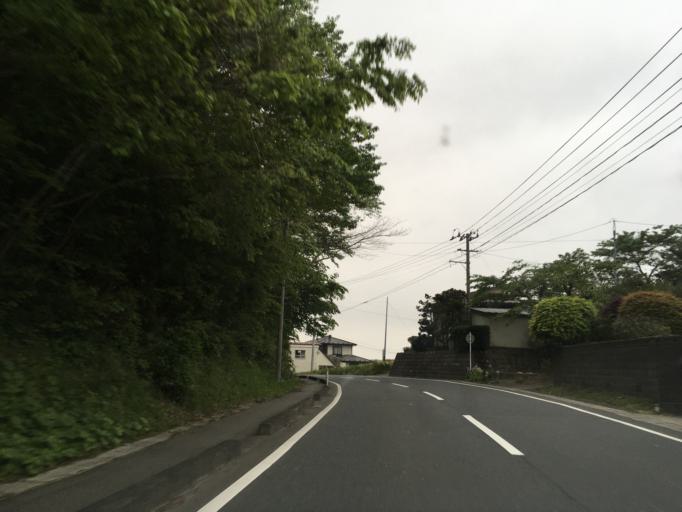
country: JP
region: Iwate
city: Ichinoseki
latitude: 38.7325
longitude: 141.3019
